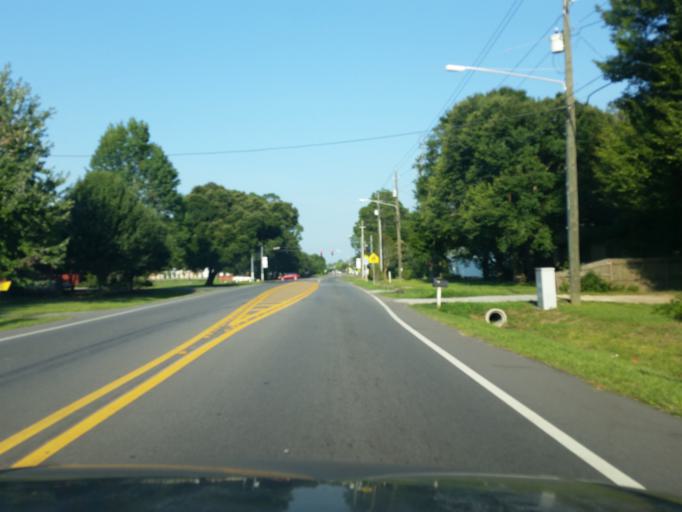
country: US
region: Alabama
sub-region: Baldwin County
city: Foley
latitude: 30.4065
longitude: -87.6933
